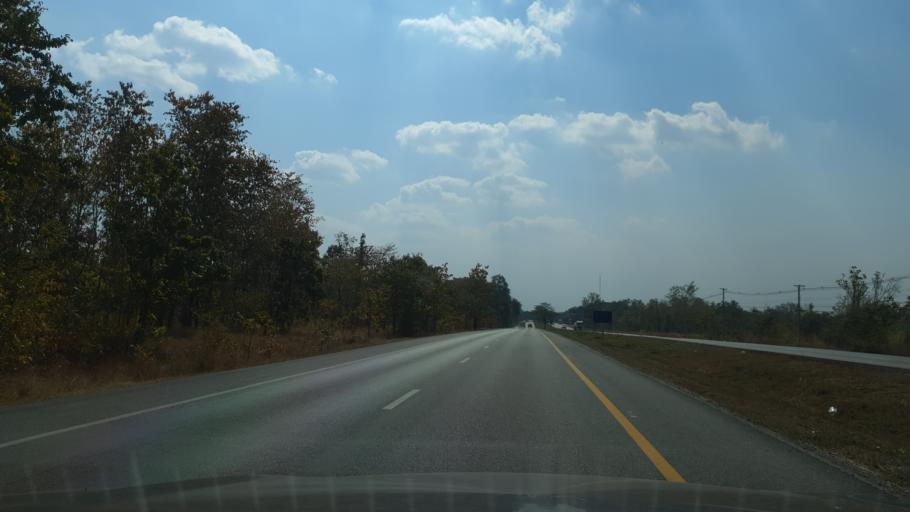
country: TH
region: Lampang
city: Mae Phrik
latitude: 17.3148
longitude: 99.1501
